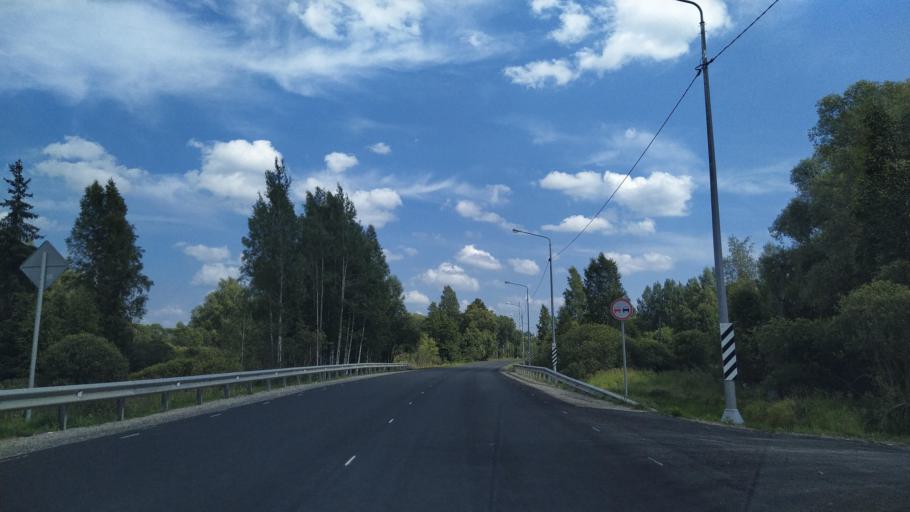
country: RU
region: Pskov
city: Porkhov
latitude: 57.7273
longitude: 29.1641
